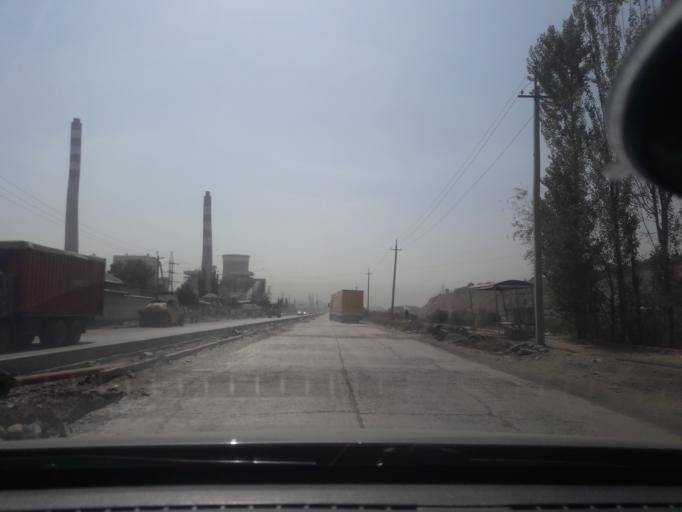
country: TJ
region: Dushanbe
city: Dushanbe
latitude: 38.6153
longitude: 68.7688
